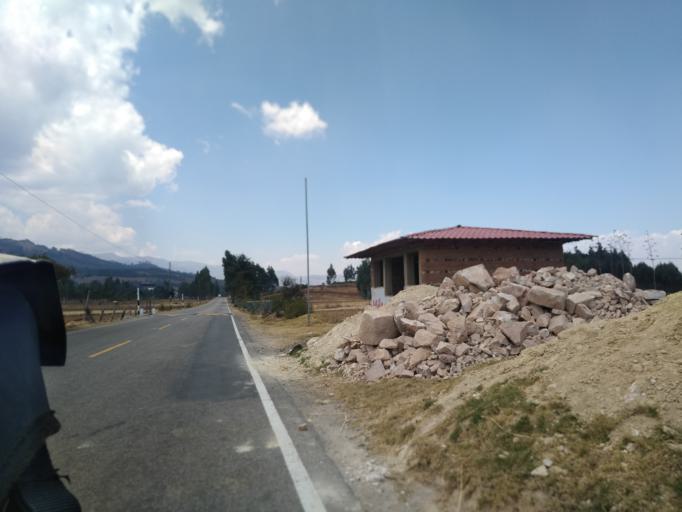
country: PE
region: Cajamarca
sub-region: San Marcos
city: San Marcos
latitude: -7.2797
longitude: -78.2355
